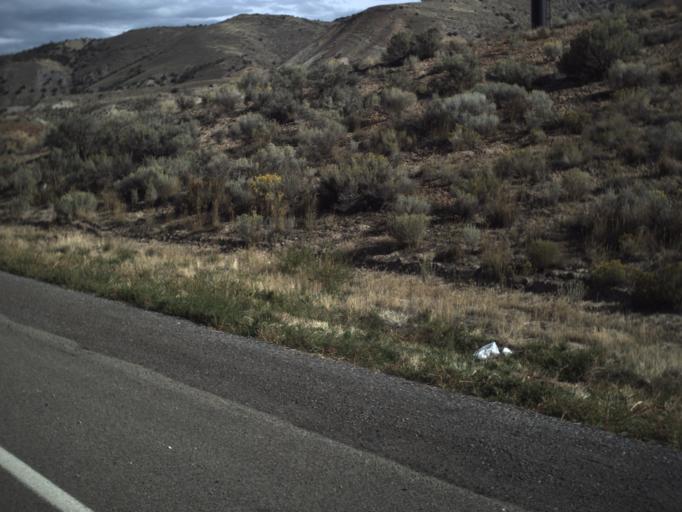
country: US
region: Utah
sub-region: Sevier County
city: Salina
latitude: 38.9331
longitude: -111.8531
